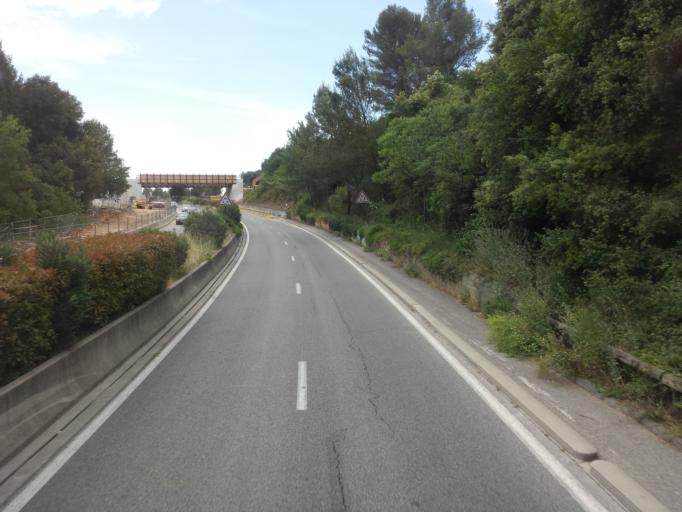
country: FR
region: Provence-Alpes-Cote d'Azur
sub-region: Departement des Alpes-Maritimes
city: Biot
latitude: 43.6071
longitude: 7.0816
